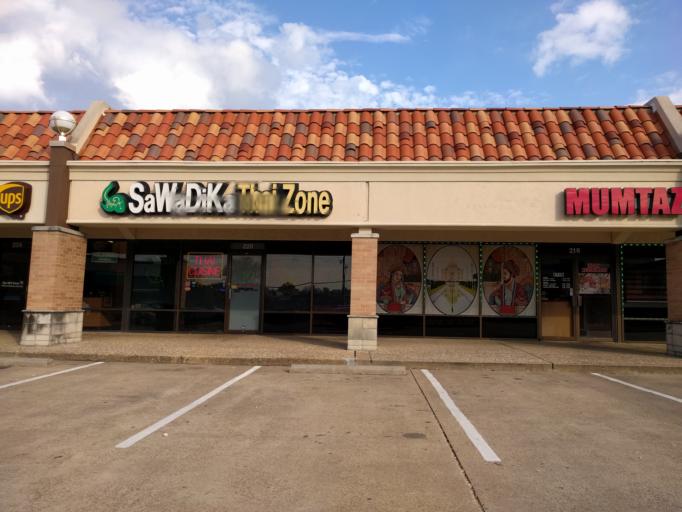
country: US
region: Texas
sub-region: Dallas County
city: Richardson
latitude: 32.9761
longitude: -96.7208
